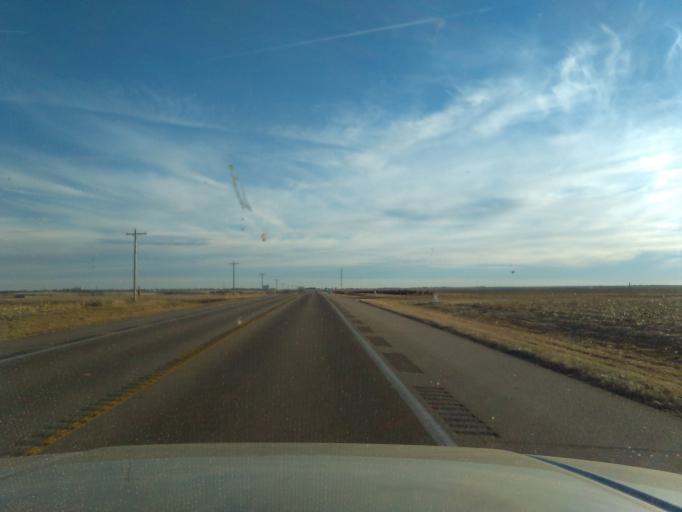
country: US
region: Kansas
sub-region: Logan County
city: Oakley
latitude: 39.1731
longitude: -100.8704
